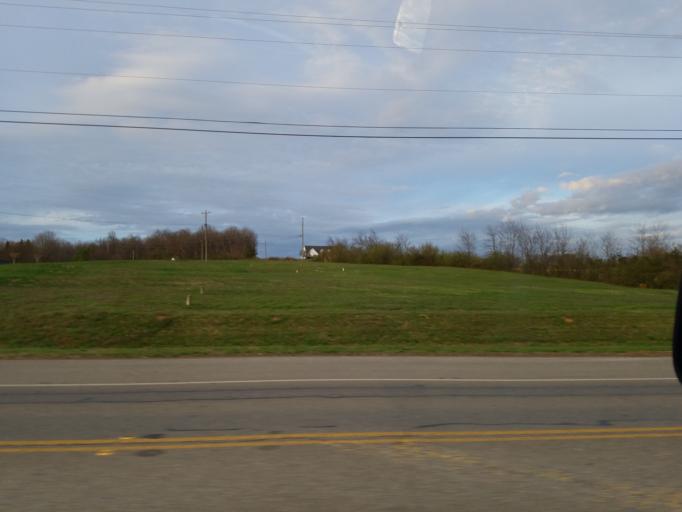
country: US
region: Georgia
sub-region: Pickens County
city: Jasper
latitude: 34.4714
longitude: -84.5172
